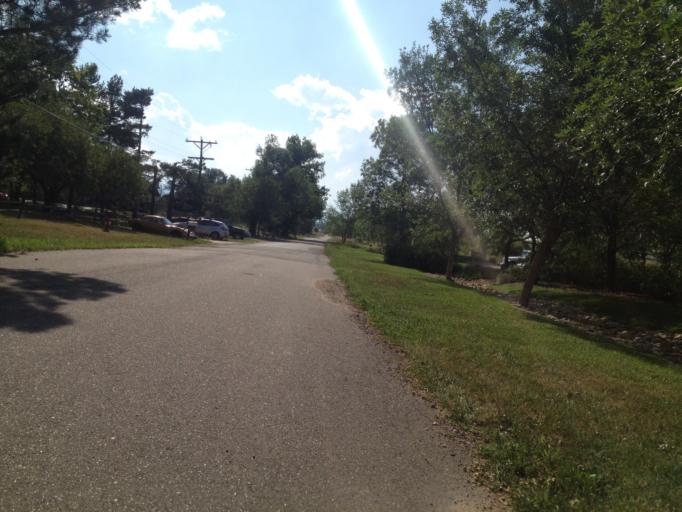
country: US
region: Colorado
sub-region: Boulder County
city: Superior
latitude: 39.9626
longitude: -105.1716
